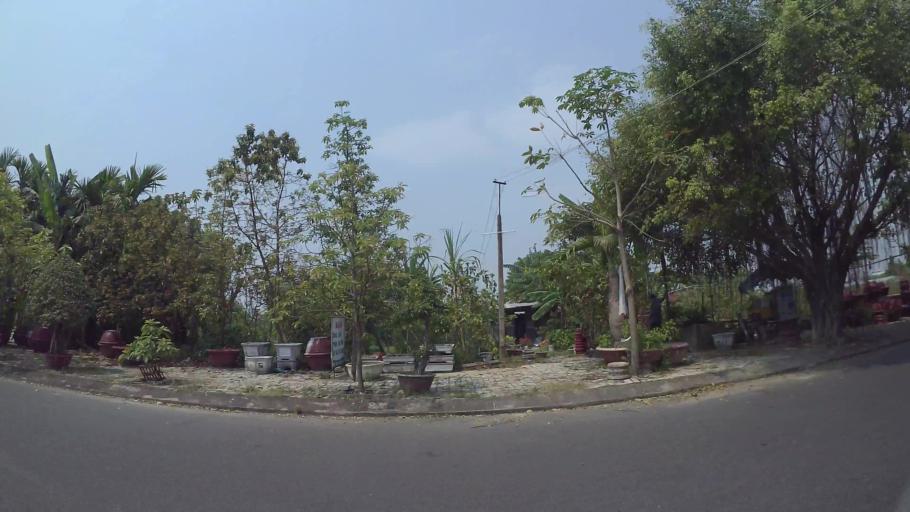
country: VN
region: Da Nang
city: Cam Le
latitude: 15.9896
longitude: 108.2137
